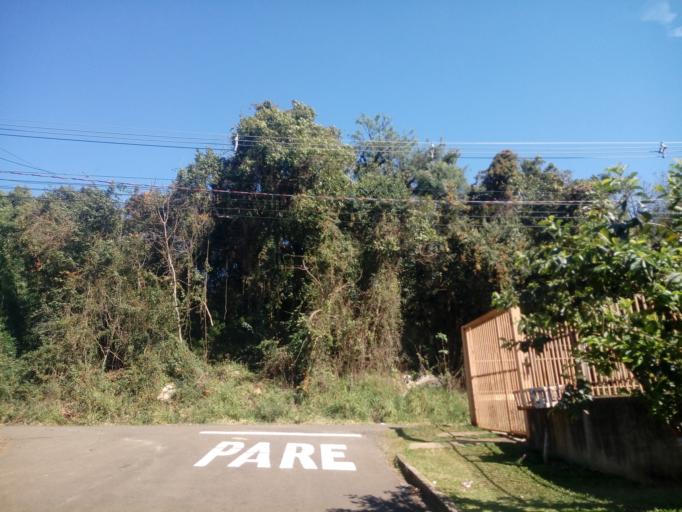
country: BR
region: Santa Catarina
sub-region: Chapeco
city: Chapeco
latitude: -27.0924
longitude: -52.6750
